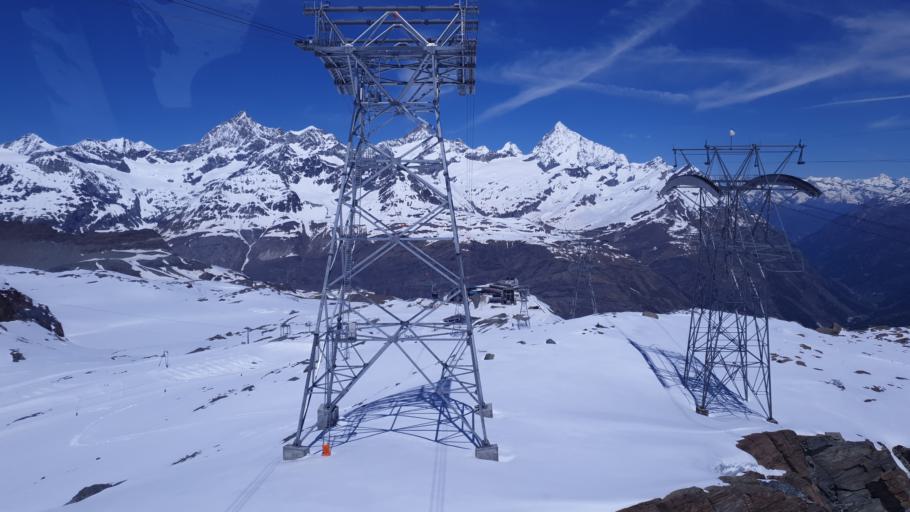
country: CH
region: Valais
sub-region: Visp District
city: Zermatt
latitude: 45.9621
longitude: 7.7237
